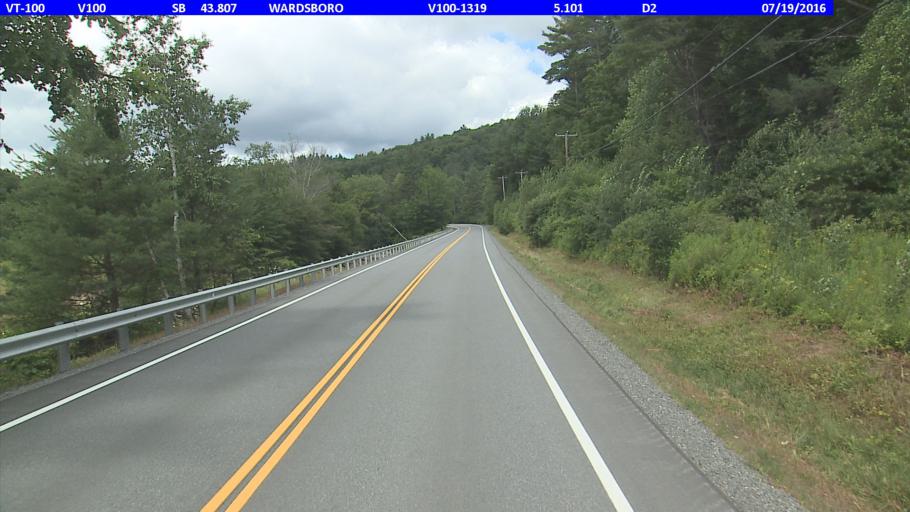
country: US
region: Vermont
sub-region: Windham County
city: Dover
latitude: 43.0719
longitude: -72.8633
